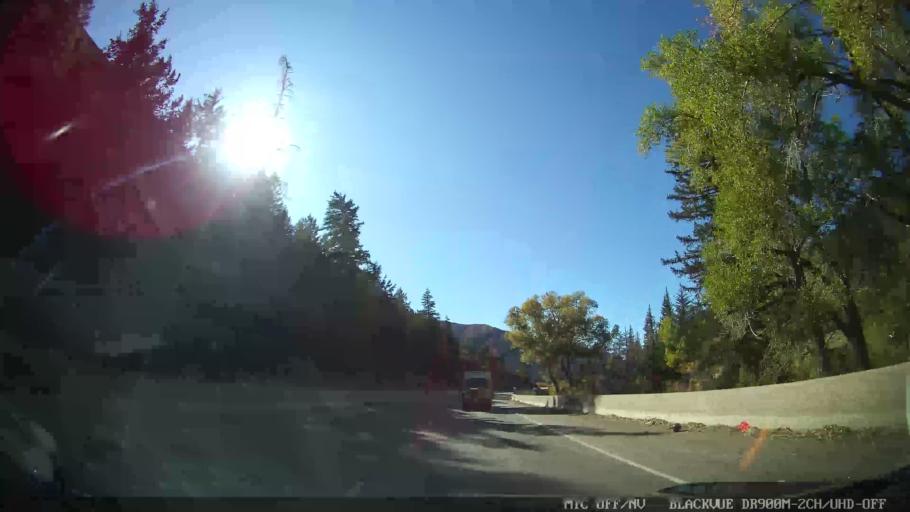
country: US
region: Colorado
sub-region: Eagle County
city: Basalt
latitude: 39.3291
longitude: -106.9683
